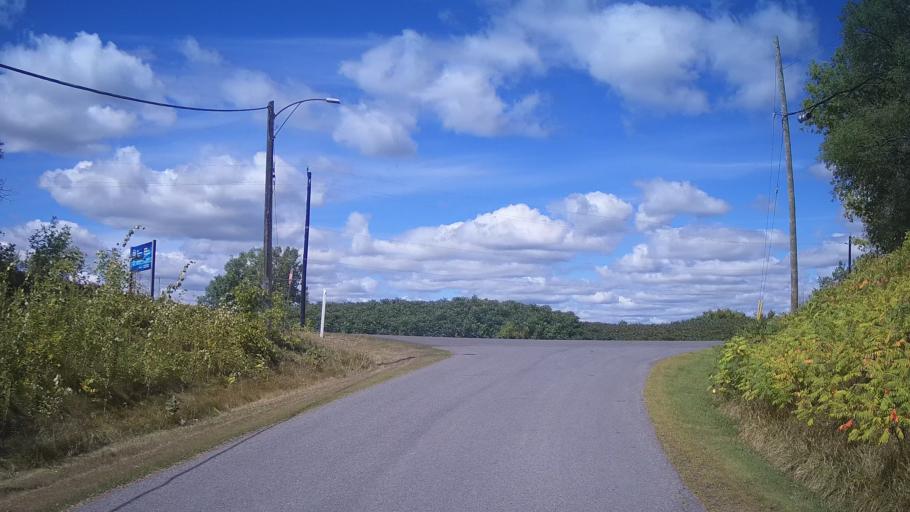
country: US
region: New York
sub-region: St. Lawrence County
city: Ogdensburg
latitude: 44.8330
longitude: -75.3133
